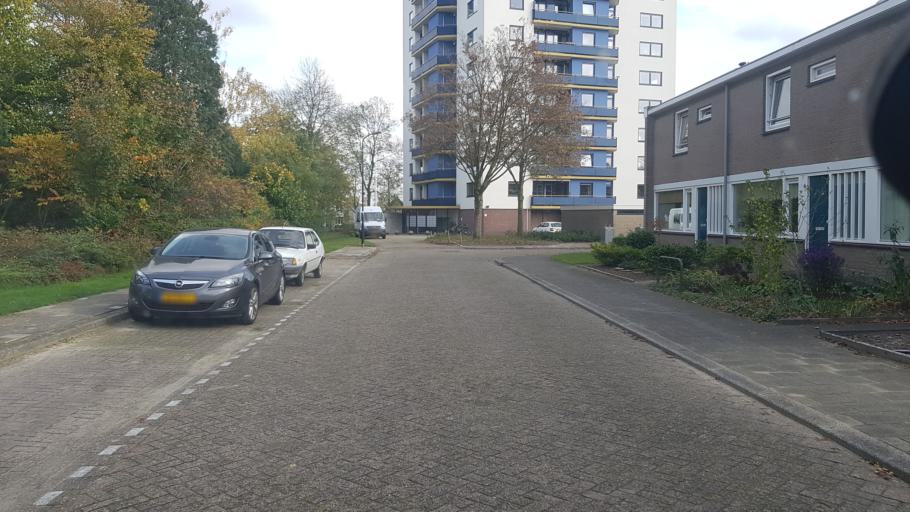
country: NL
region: Gelderland
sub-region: Gemeente Apeldoorn
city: Apeldoorn
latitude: 52.2288
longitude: 5.9659
